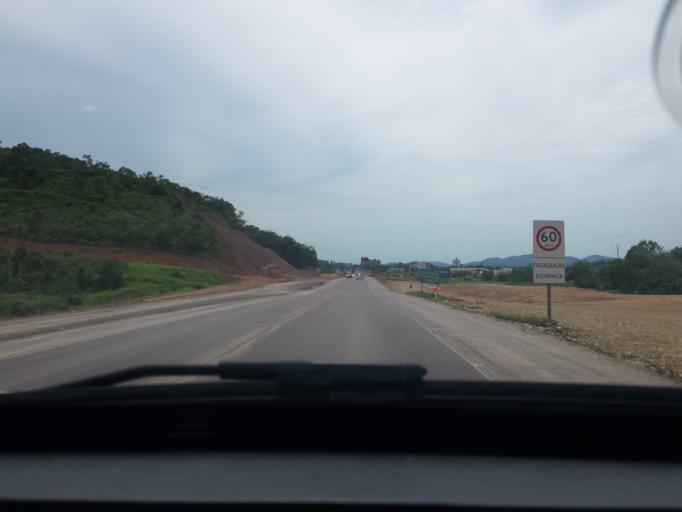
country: BR
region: Santa Catarina
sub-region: Gaspar
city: Gaspar
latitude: -26.9136
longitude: -48.9649
